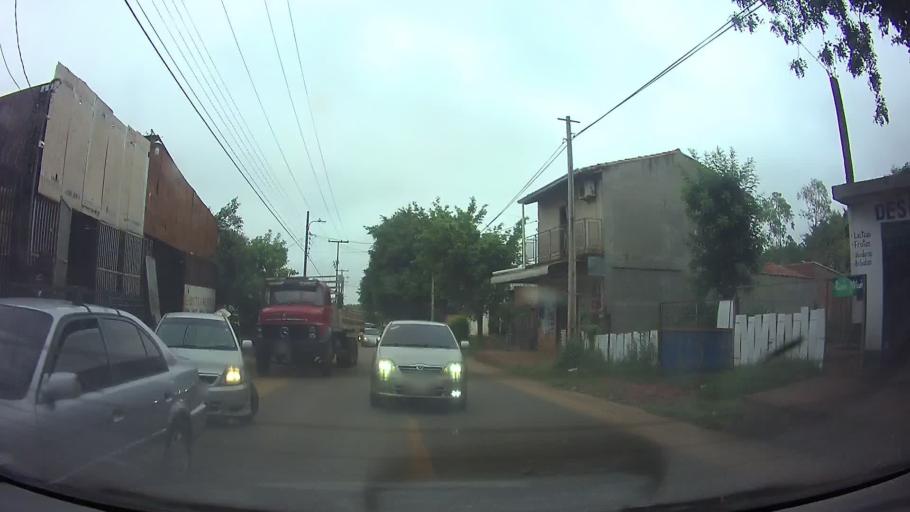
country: PY
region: Central
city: San Lorenzo
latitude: -25.3092
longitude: -57.4912
